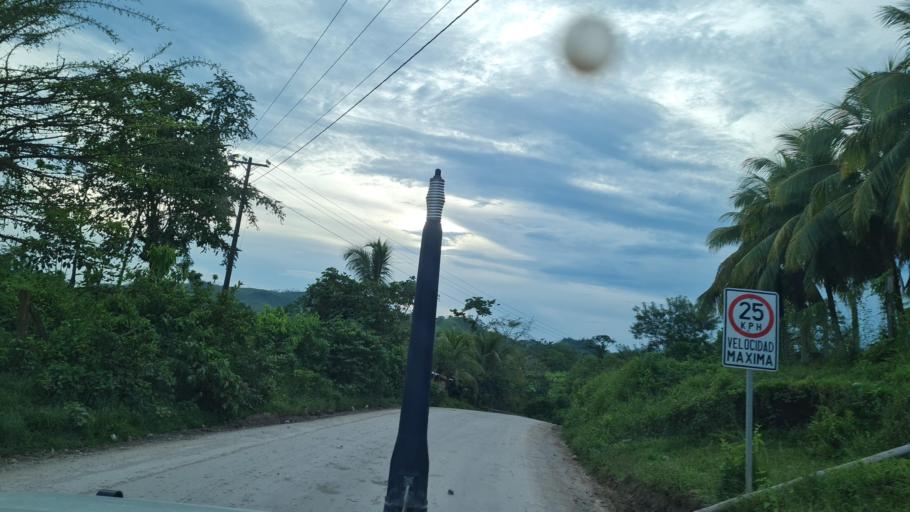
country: NI
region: Atlantico Norte (RAAN)
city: Siuna
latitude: 13.6861
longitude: -84.6172
